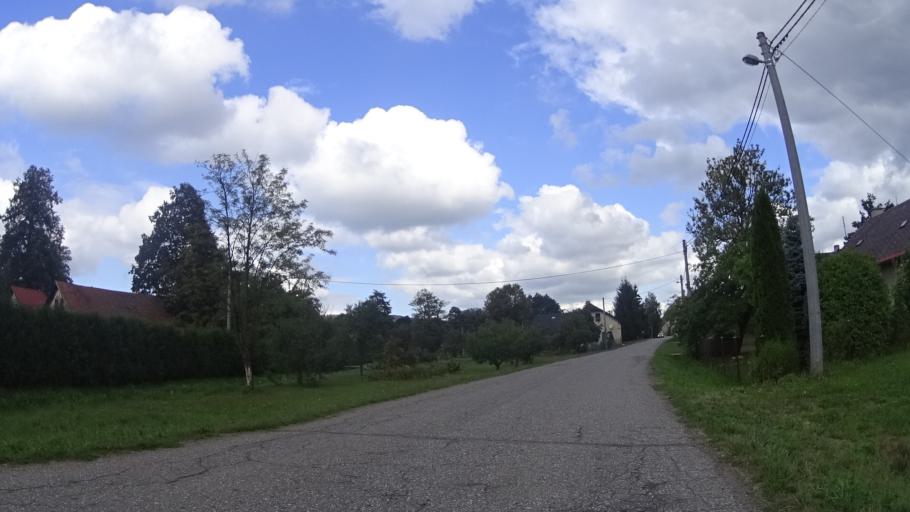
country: CZ
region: Pardubicky
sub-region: Okres Usti nad Orlici
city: Lanskroun
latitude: 49.9217
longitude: 16.5553
